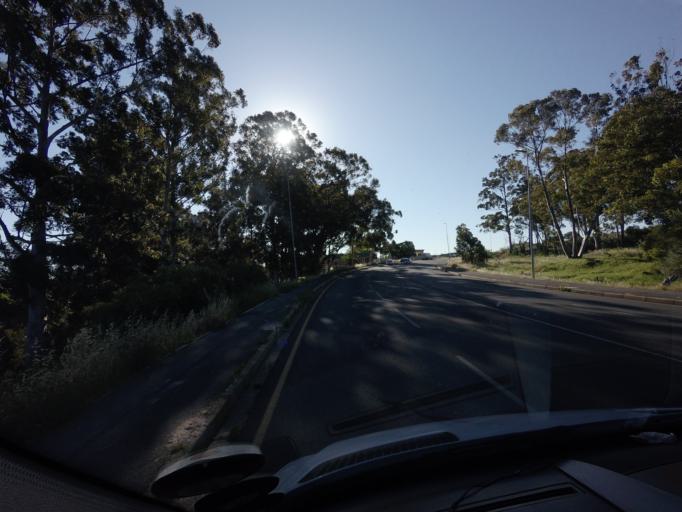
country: ZA
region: Western Cape
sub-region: Cape Winelands District Municipality
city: Stellenbosch
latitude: -33.9228
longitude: 18.8670
